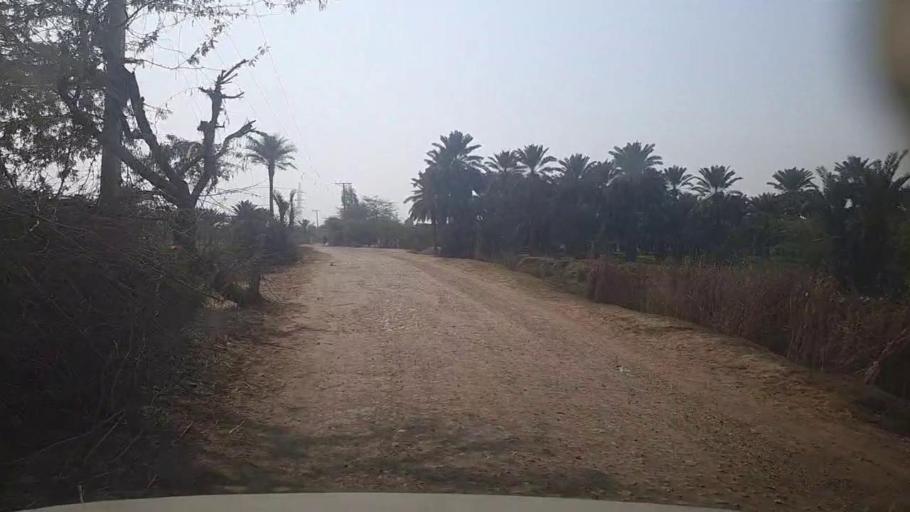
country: PK
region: Sindh
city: Kot Diji
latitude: 27.3596
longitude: 68.7414
